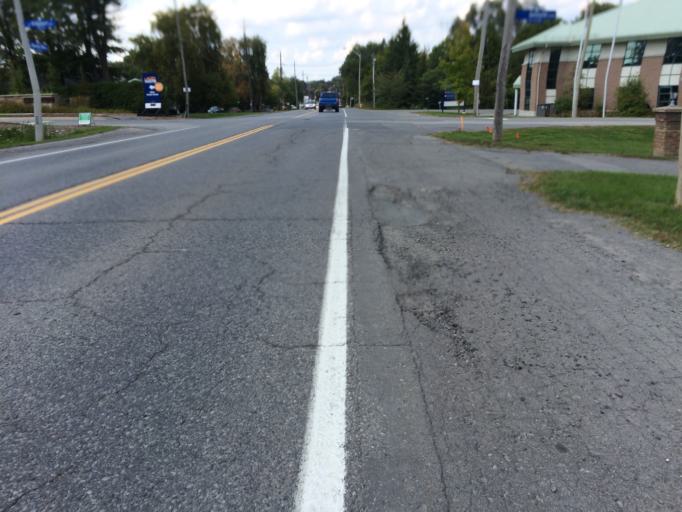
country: CA
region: Ontario
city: Bells Corners
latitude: 45.2190
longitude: -75.6739
